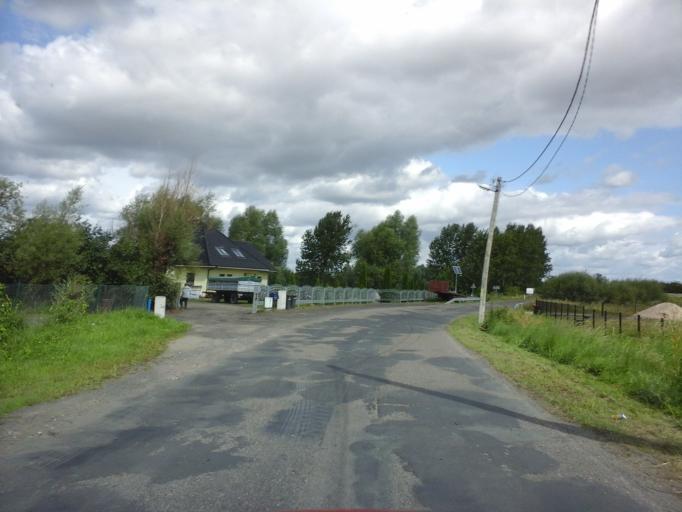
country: PL
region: West Pomeranian Voivodeship
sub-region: Powiat stargardzki
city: Kobylanka
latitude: 53.3341
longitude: 14.9420
